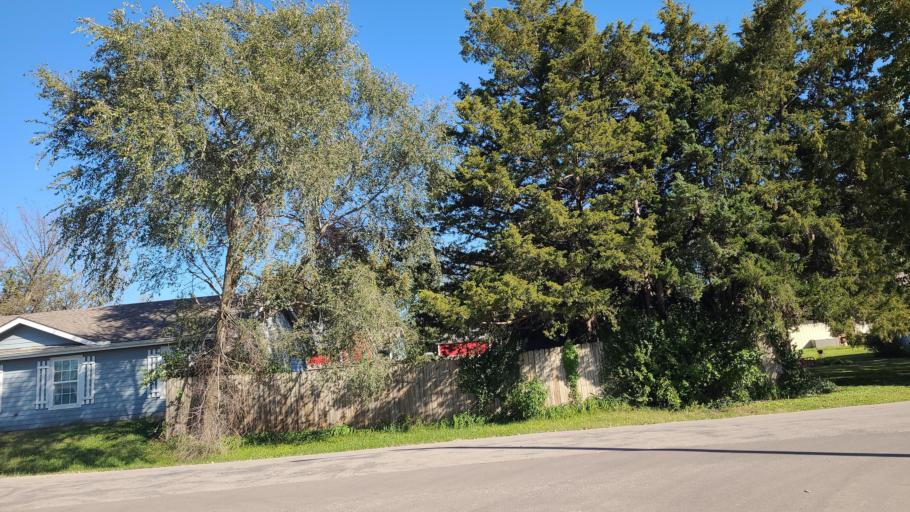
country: US
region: Kansas
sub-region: Douglas County
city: Lawrence
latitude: 38.9505
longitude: -95.2259
